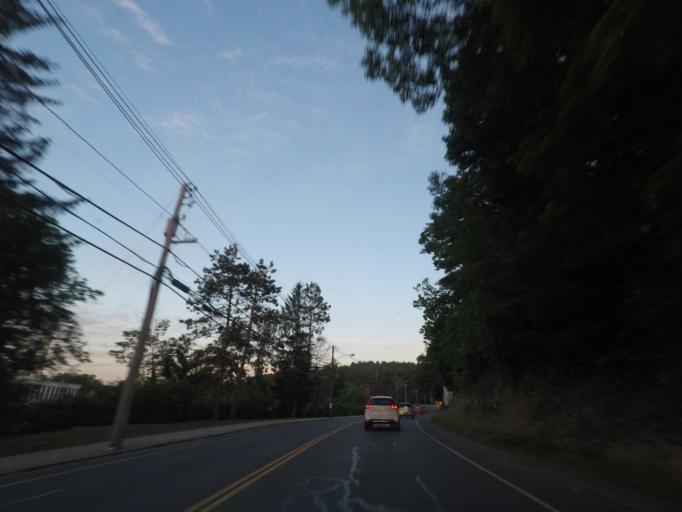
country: US
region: Massachusetts
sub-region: Worcester County
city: Southbridge
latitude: 42.0721
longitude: -72.0245
